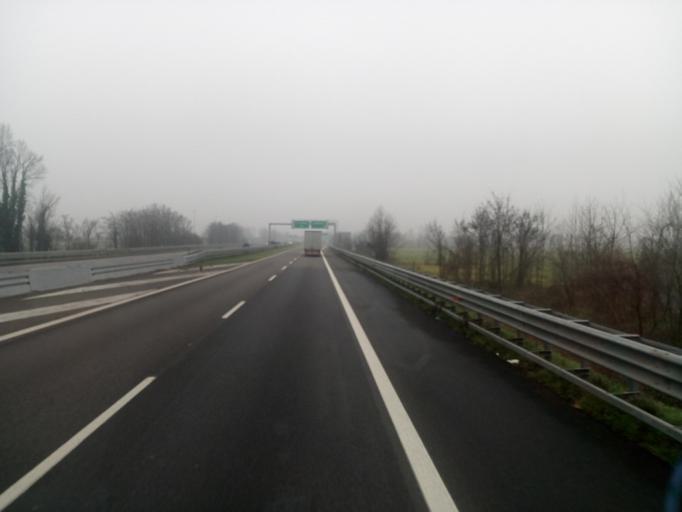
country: IT
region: Lombardy
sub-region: Provincia di Brescia
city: Manerbio
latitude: 45.3712
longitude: 10.1724
